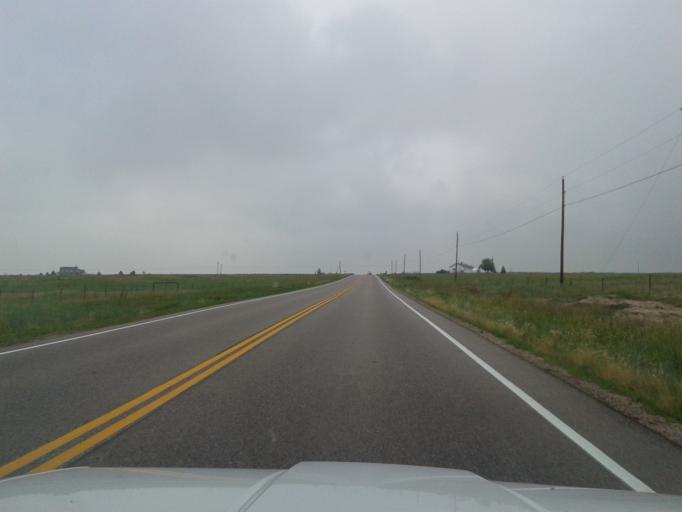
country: US
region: Colorado
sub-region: Elbert County
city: Ponderosa Park
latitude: 39.3372
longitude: -104.7340
